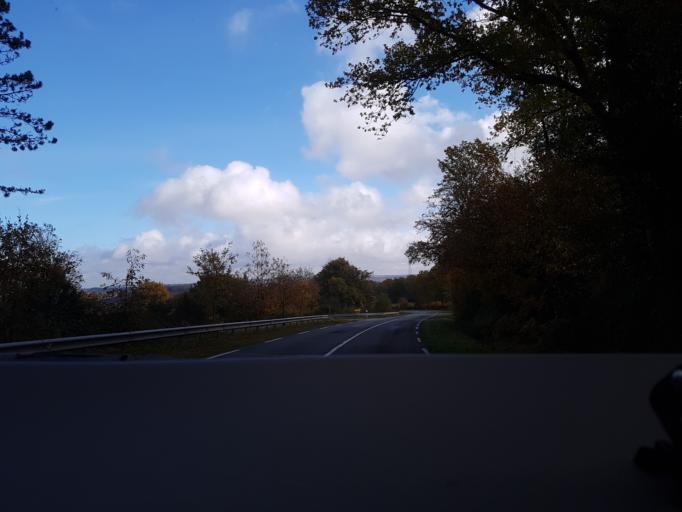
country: FR
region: Lower Normandy
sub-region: Departement de l'Orne
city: Domfront
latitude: 48.5969
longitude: -0.6218
